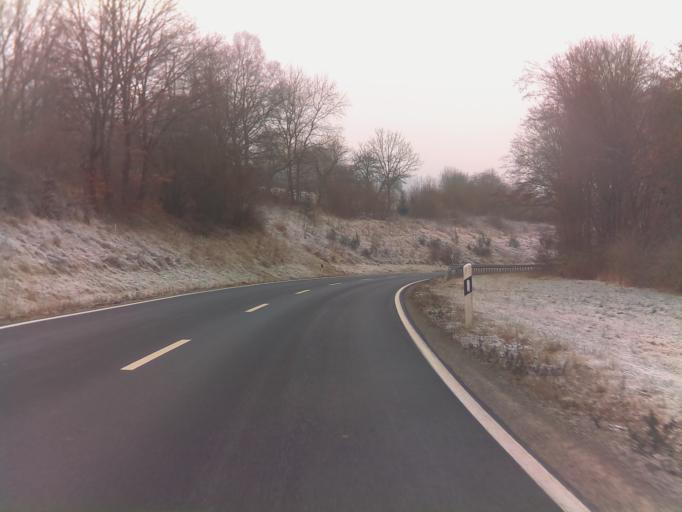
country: DE
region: Bavaria
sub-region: Regierungsbezirk Unterfranken
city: Zeitlofs
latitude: 50.2625
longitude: 9.6909
